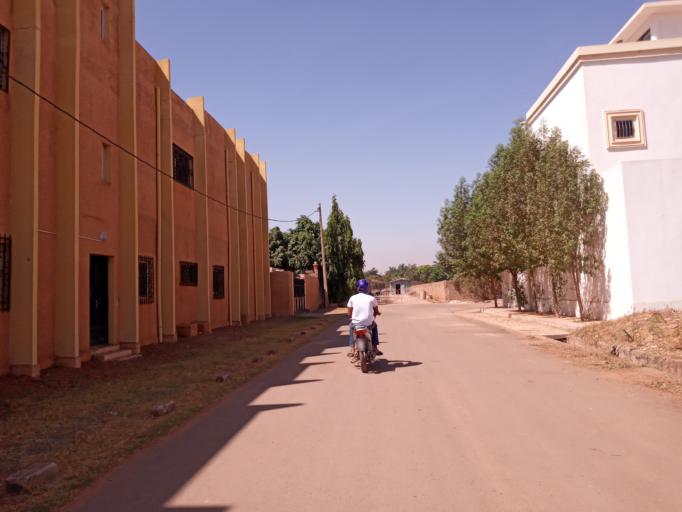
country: ML
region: Bamako
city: Bamako
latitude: 12.6028
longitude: -8.0476
